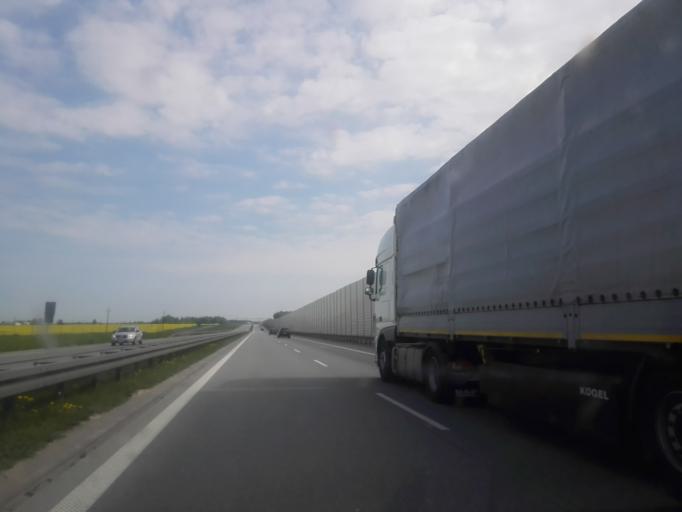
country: PL
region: Lodz Voivodeship
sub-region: Powiat skierniewicki
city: Kowiesy
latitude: 51.8514
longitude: 20.3700
